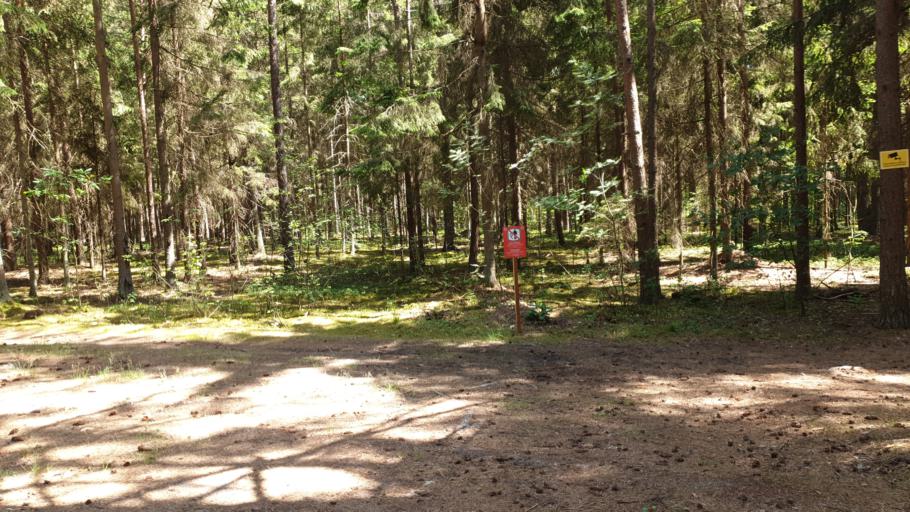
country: LT
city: Grigiskes
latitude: 54.7770
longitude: 24.9931
